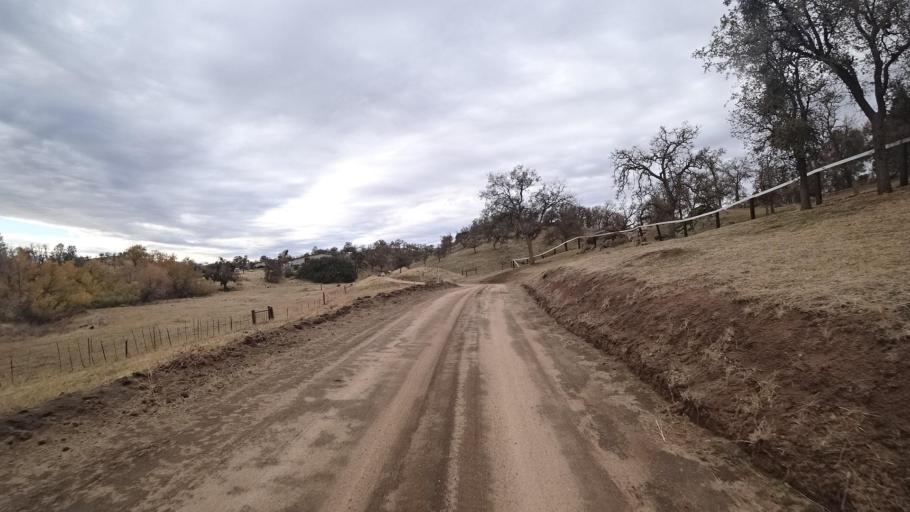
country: US
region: California
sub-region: Kern County
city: Stallion Springs
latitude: 35.1103
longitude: -118.6755
